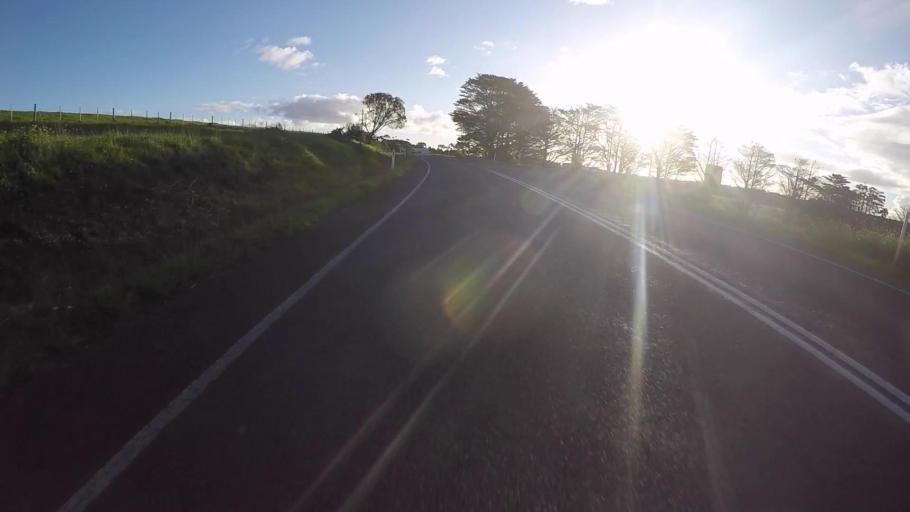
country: AU
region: Victoria
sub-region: Greater Geelong
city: Wandana Heights
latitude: -38.1688
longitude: 144.2142
